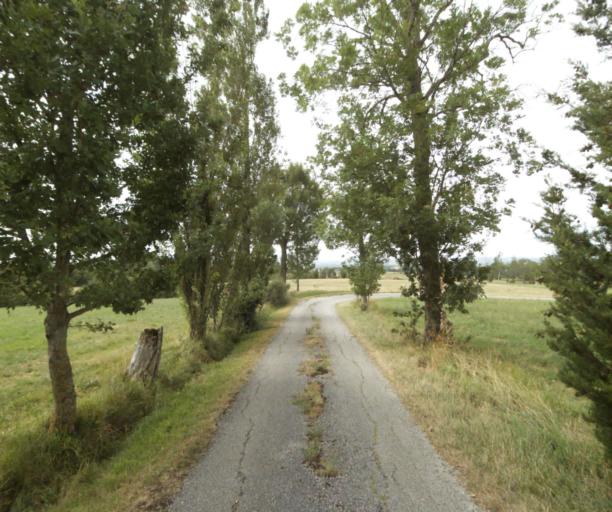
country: FR
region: Midi-Pyrenees
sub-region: Departement du Tarn
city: Soreze
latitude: 43.4610
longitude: 2.0832
